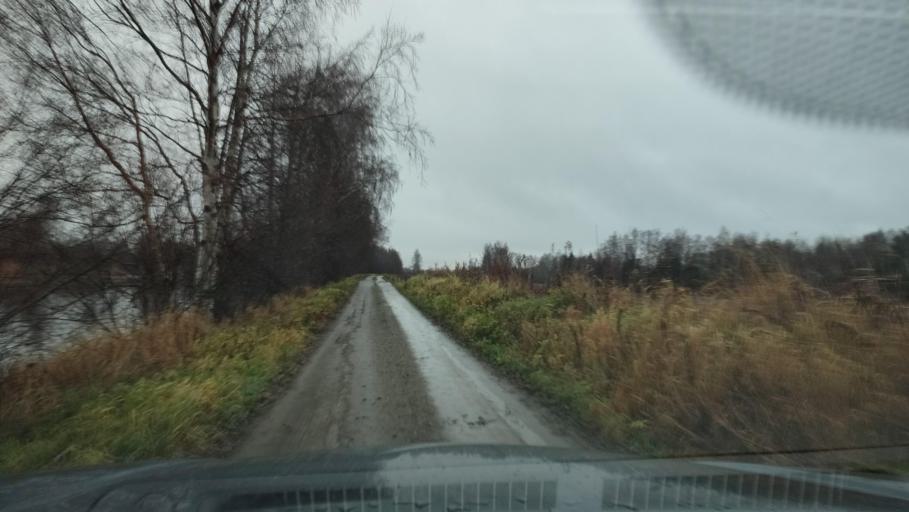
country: FI
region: Ostrobothnia
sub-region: Sydosterbotten
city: Kristinestad
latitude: 62.2305
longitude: 21.4500
